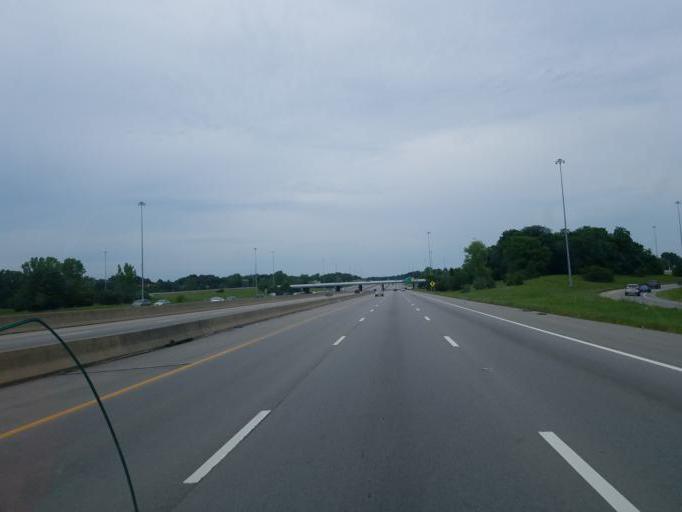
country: US
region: Ohio
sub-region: Franklin County
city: Reynoldsburg
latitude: 39.9510
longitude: -82.8447
